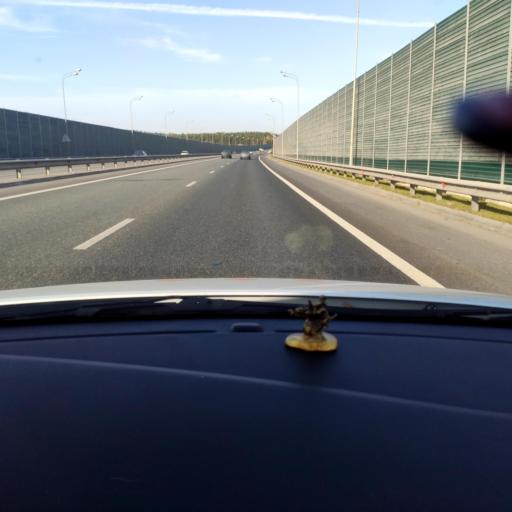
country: RU
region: Tatarstan
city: Osinovo
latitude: 55.8175
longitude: 48.8432
